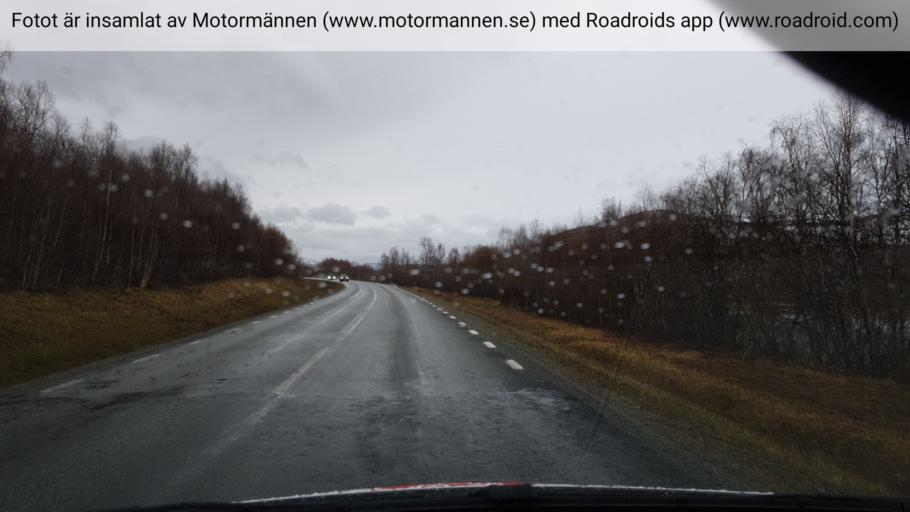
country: NO
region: Nordland
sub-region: Rana
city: Mo i Rana
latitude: 65.7983
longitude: 15.0974
